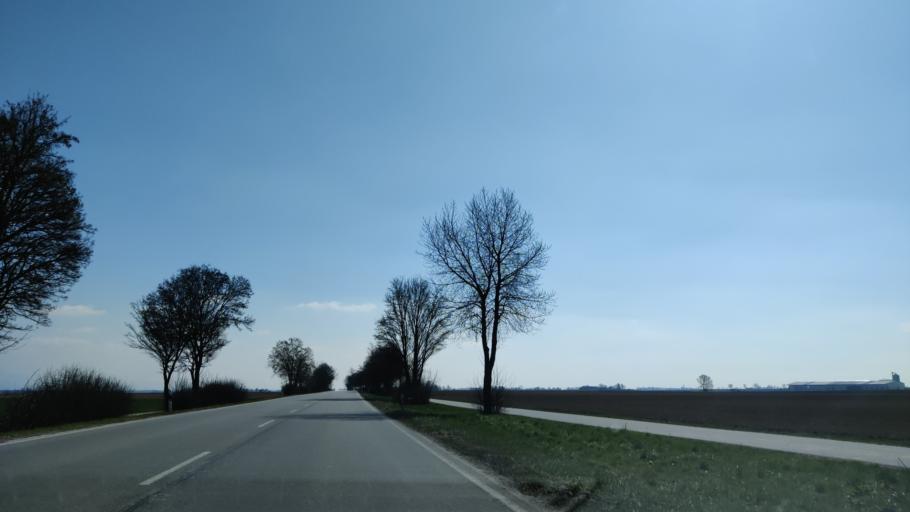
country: DE
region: Bavaria
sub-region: Lower Bavaria
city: Alterhofen
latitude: 48.8418
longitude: 12.6428
